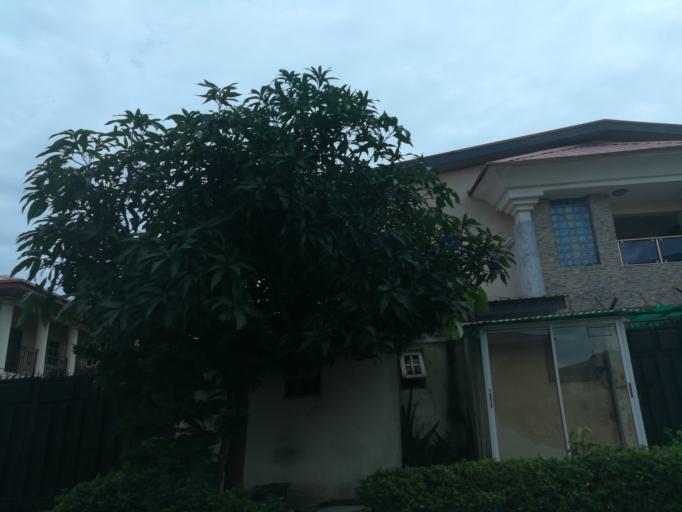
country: NG
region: Lagos
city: Ikoyi
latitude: 6.4417
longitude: 3.4769
